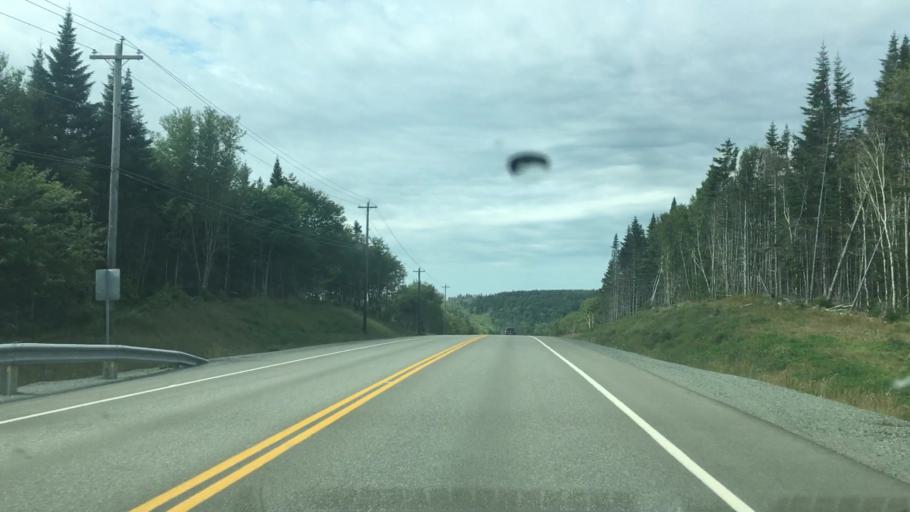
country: CA
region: Nova Scotia
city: Princeville
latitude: 45.6710
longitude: -60.7999
